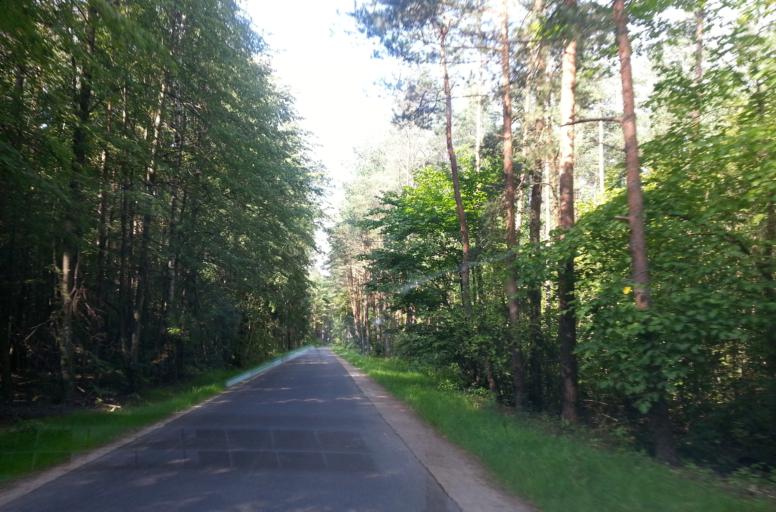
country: LT
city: Grigiskes
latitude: 54.7246
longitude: 25.0564
